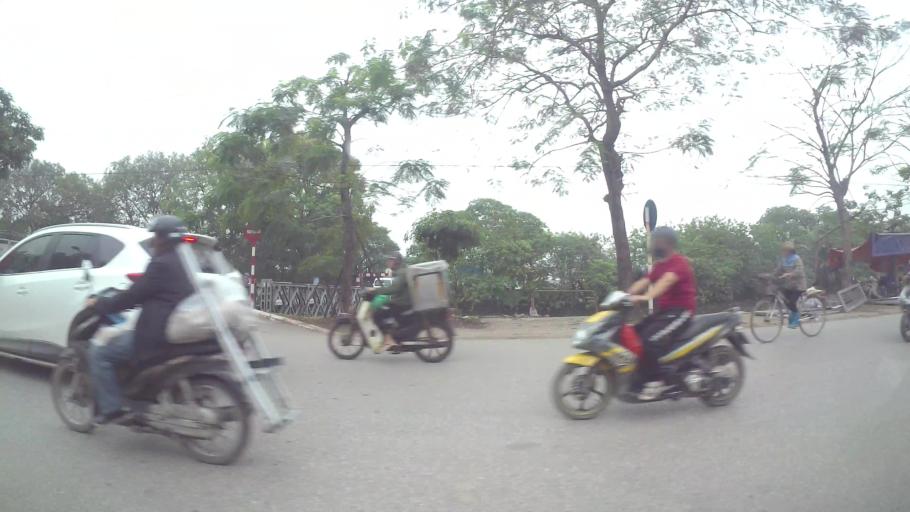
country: VN
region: Ha Noi
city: Hai BaTrung
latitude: 20.9828
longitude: 105.8640
